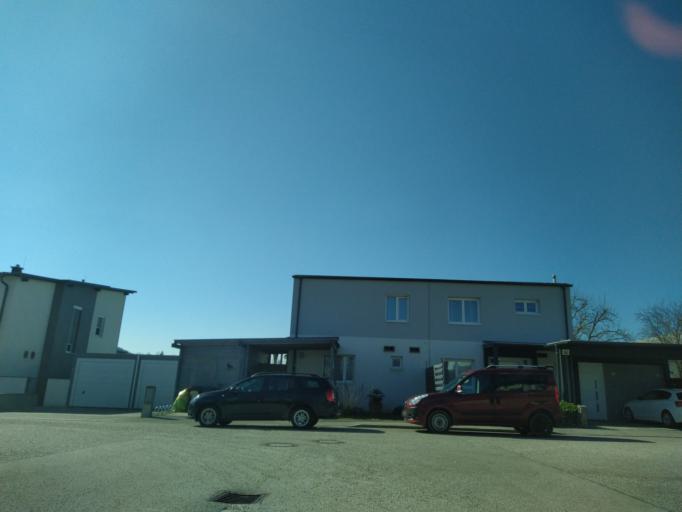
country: AT
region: Upper Austria
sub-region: Wels-Land
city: Steinhaus
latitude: 48.1435
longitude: 13.9917
